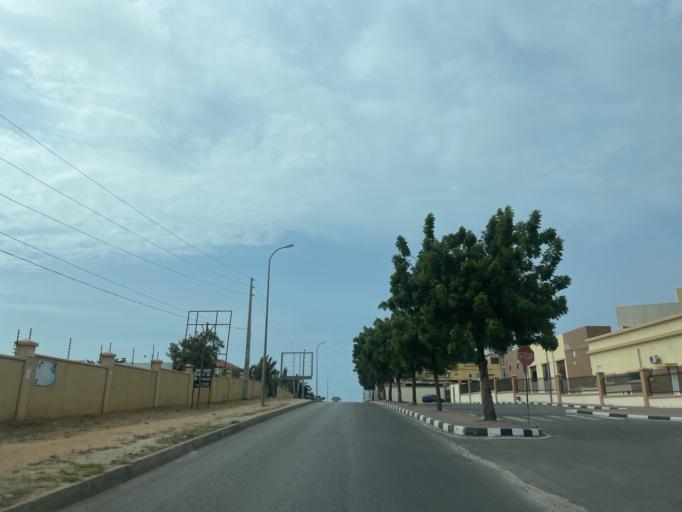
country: AO
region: Luanda
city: Luanda
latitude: -8.9212
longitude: 13.1701
